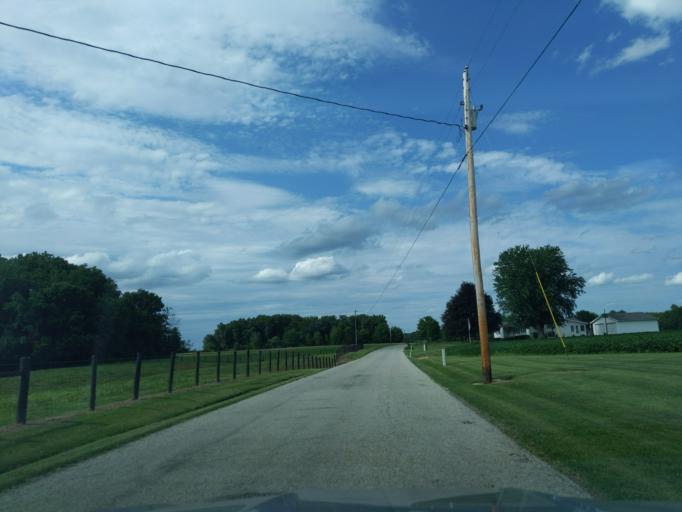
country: US
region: Indiana
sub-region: Ripley County
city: Sunman
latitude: 39.2962
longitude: -85.0900
